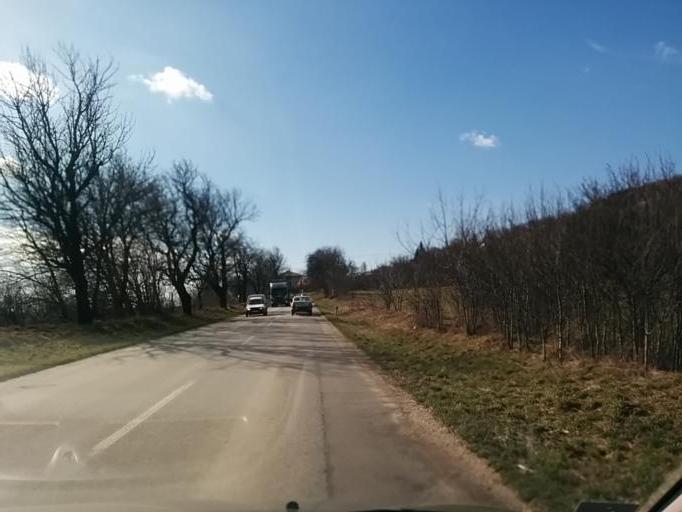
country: SK
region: Trenciansky
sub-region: Okres Nove Mesto nad Vahom
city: Nove Mesto nad Vahom
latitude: 48.7390
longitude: 17.8163
